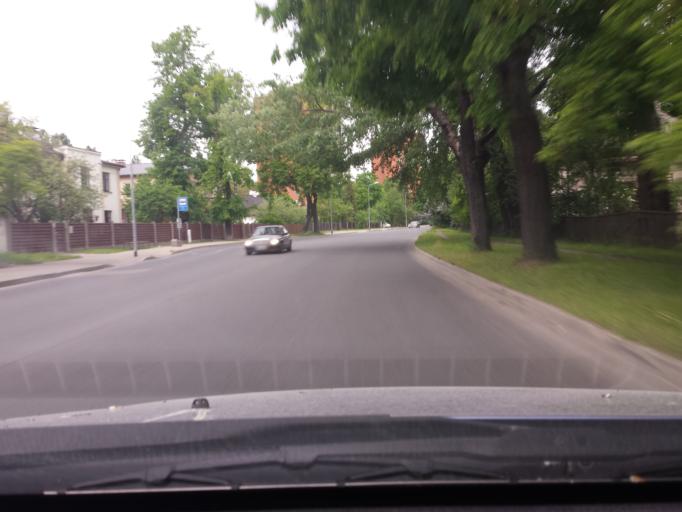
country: LV
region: Riga
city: Jaunciems
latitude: 56.9986
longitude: 24.1707
